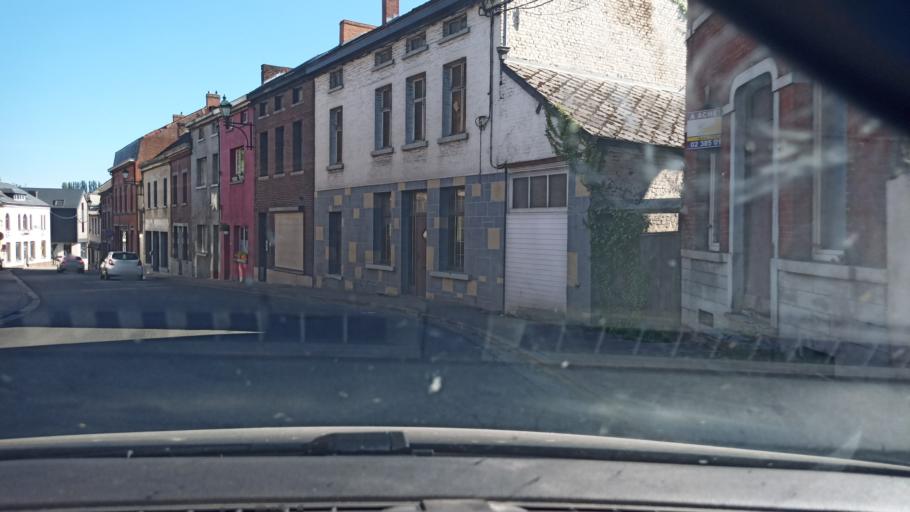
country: BE
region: Wallonia
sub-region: Province du Hainaut
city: Lobbes
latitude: 50.3481
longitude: 4.2642
